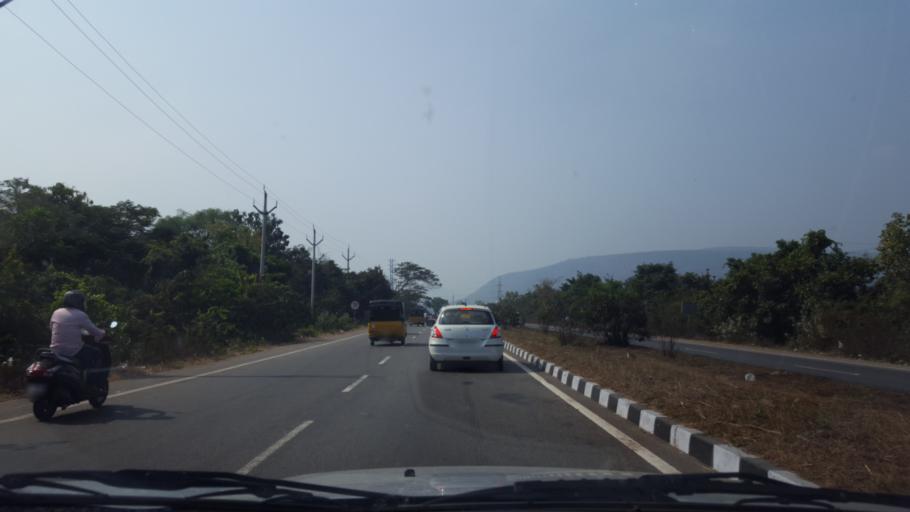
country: IN
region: Andhra Pradesh
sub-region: Vishakhapatnam
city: Bhimunipatnam
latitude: 17.8845
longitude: 83.3773
